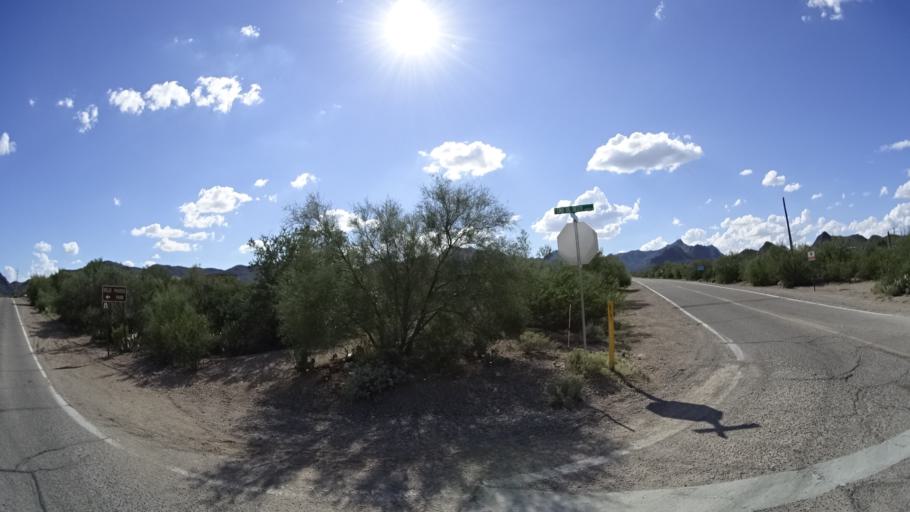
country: US
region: Arizona
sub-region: Pima County
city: Tucson Estates
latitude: 32.2426
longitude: -111.0628
